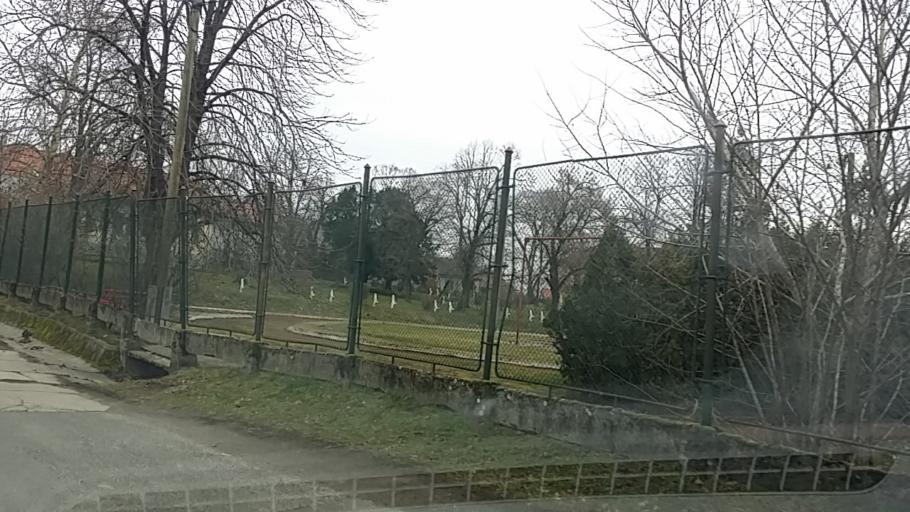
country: HU
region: Baranya
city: Dunaszekcso
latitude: 46.0853
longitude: 18.7587
